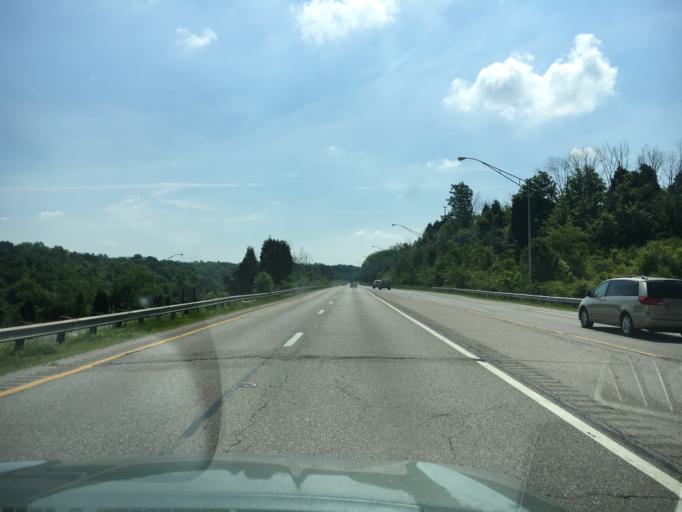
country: US
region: Ohio
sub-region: Hamilton County
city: Dent
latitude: 39.1967
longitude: -84.6585
